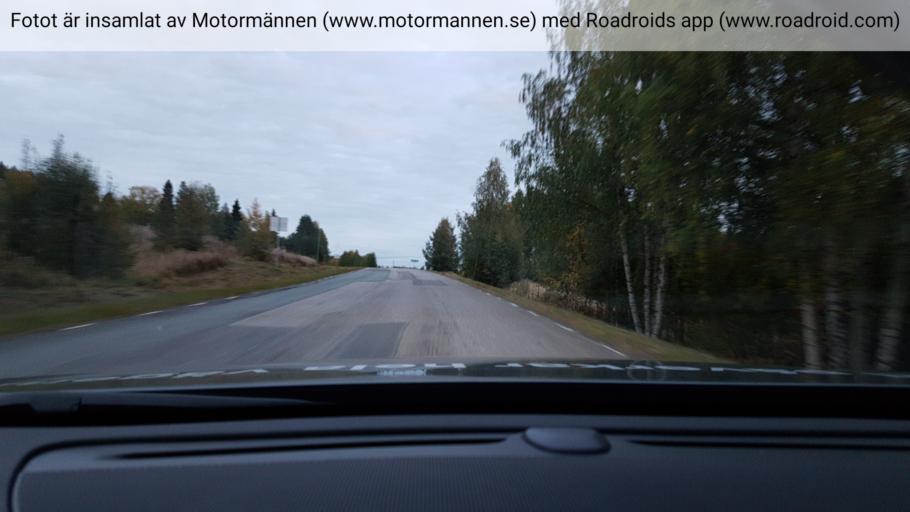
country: SE
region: Norrbotten
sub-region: Alvsbyns Kommun
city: AElvsbyn
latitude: 65.8547
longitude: 20.4334
